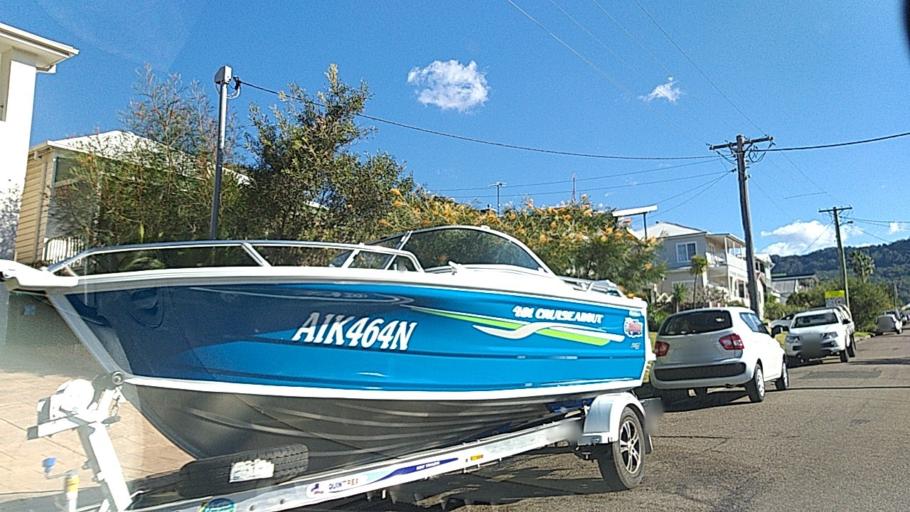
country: AU
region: New South Wales
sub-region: Wollongong
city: Bulli
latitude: -34.3384
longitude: 150.9181
